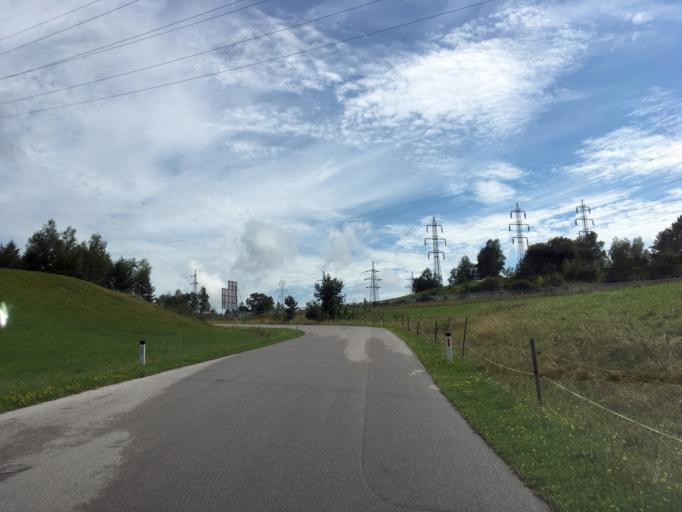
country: SI
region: Jesenice
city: Slovenski Javornik
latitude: 46.4143
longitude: 14.1029
